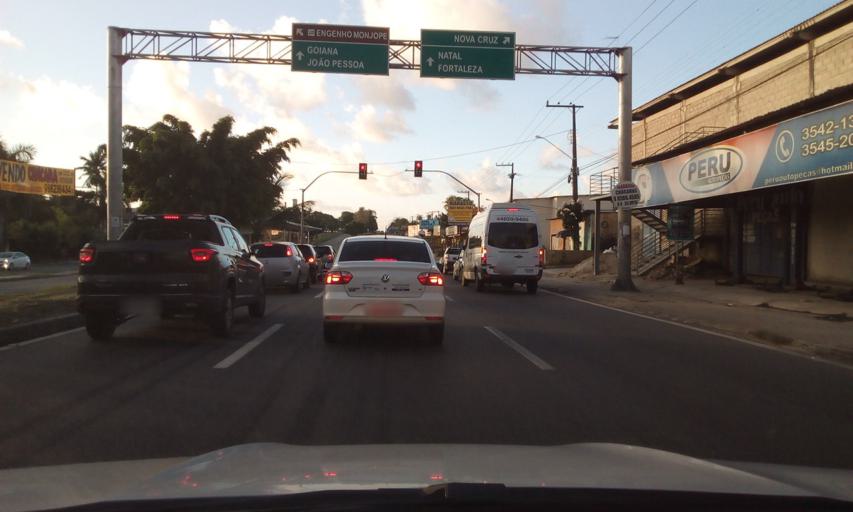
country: BR
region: Pernambuco
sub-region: Igarassu
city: Igarassu
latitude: -7.8669
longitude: -34.9069
